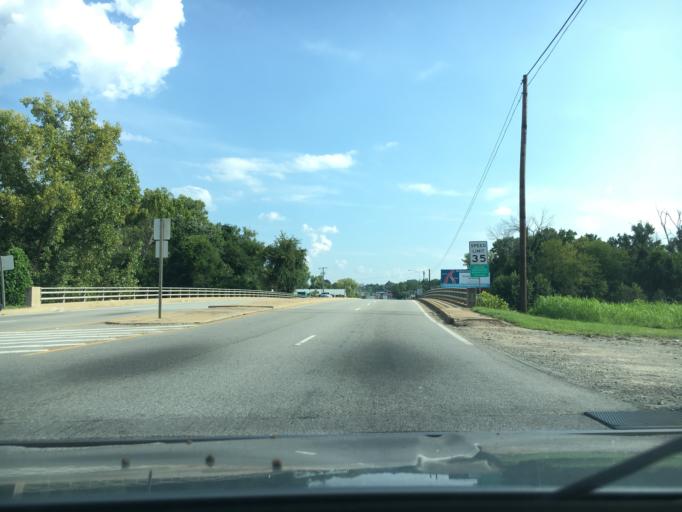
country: US
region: Virginia
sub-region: Halifax County
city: South Boston
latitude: 36.6946
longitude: -78.9007
